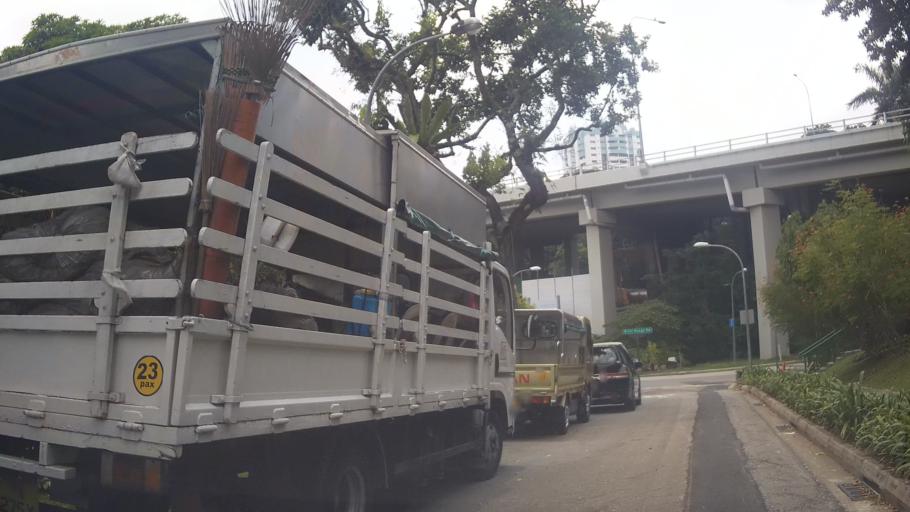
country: SG
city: Singapore
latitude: 1.3412
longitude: 103.7803
